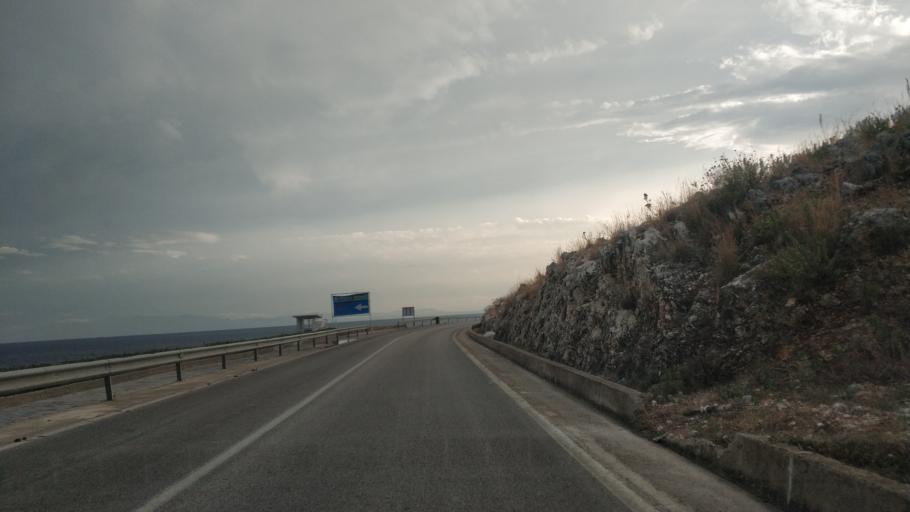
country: AL
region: Vlore
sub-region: Rrethi i Vlores
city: Himare
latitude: 40.0483
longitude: 19.8114
